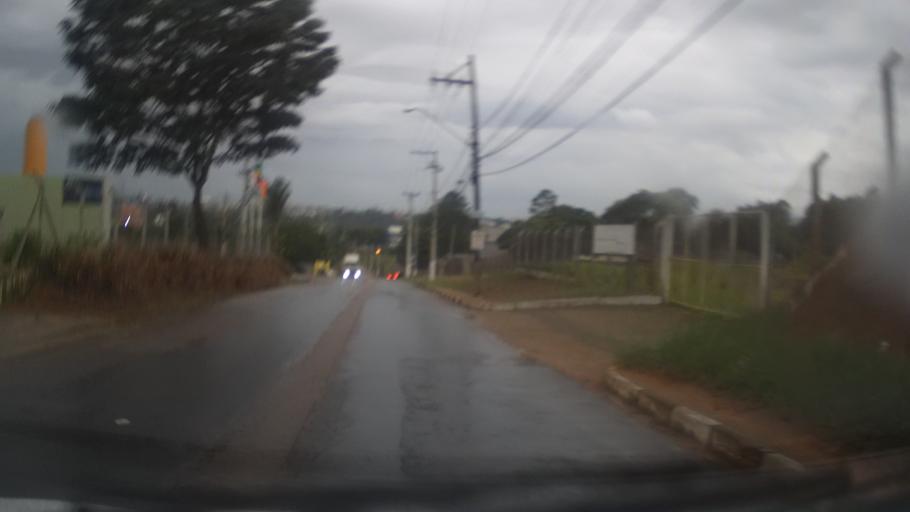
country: BR
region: Sao Paulo
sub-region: Itupeva
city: Itupeva
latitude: -23.1651
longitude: -47.0247
